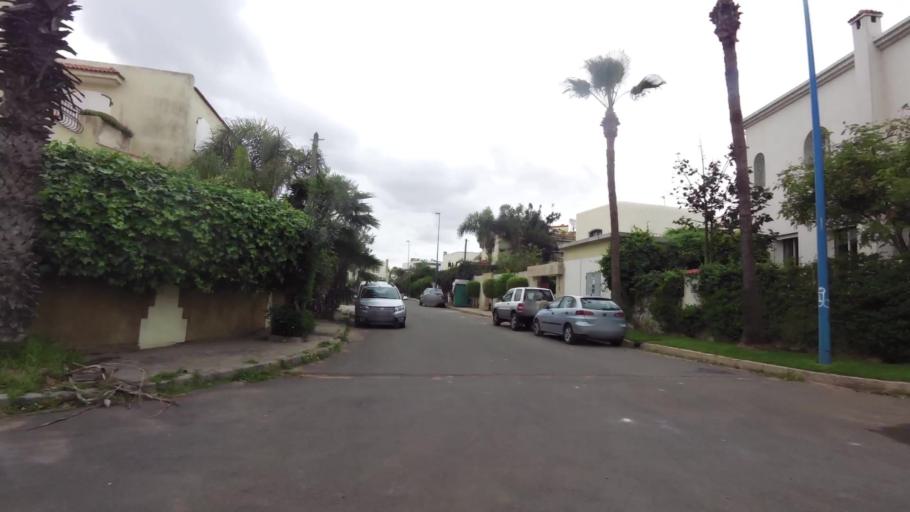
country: MA
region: Grand Casablanca
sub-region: Casablanca
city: Casablanca
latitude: 33.6005
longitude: -7.6535
